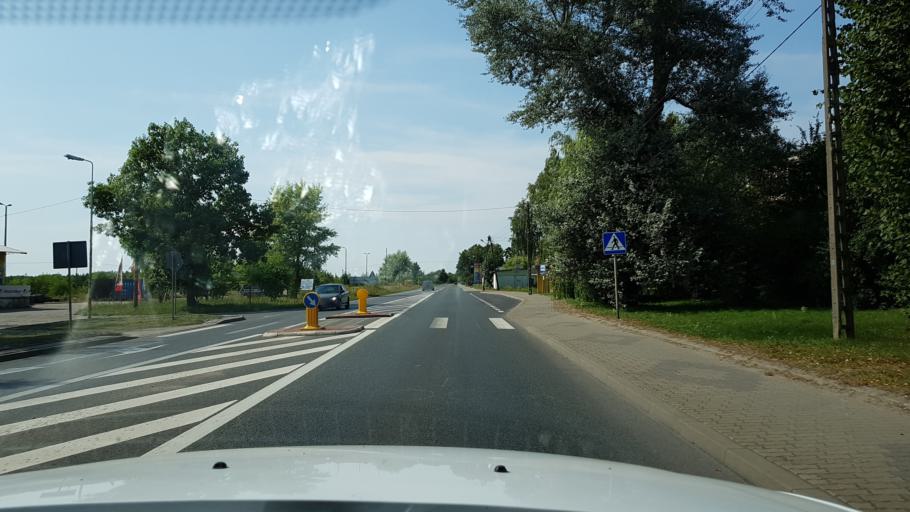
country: PL
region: West Pomeranian Voivodeship
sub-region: Powiat pyrzycki
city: Lipiany
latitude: 53.0027
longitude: 14.9538
